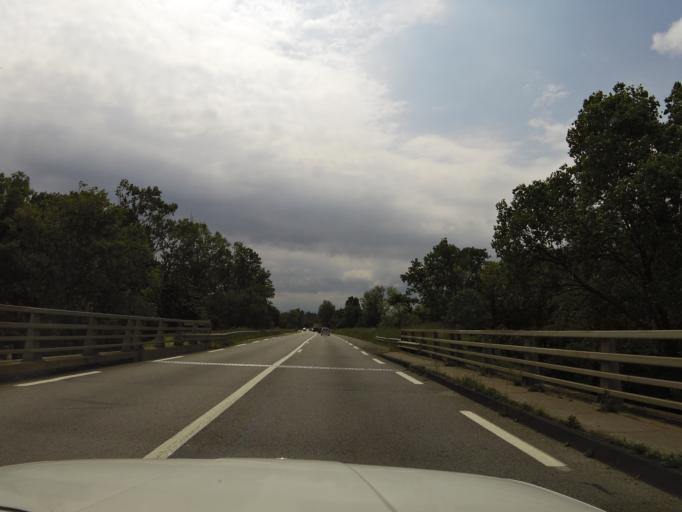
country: FR
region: Rhone-Alpes
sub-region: Departement de la Drome
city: La Roche-de-Glun
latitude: 44.9973
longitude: 4.8751
